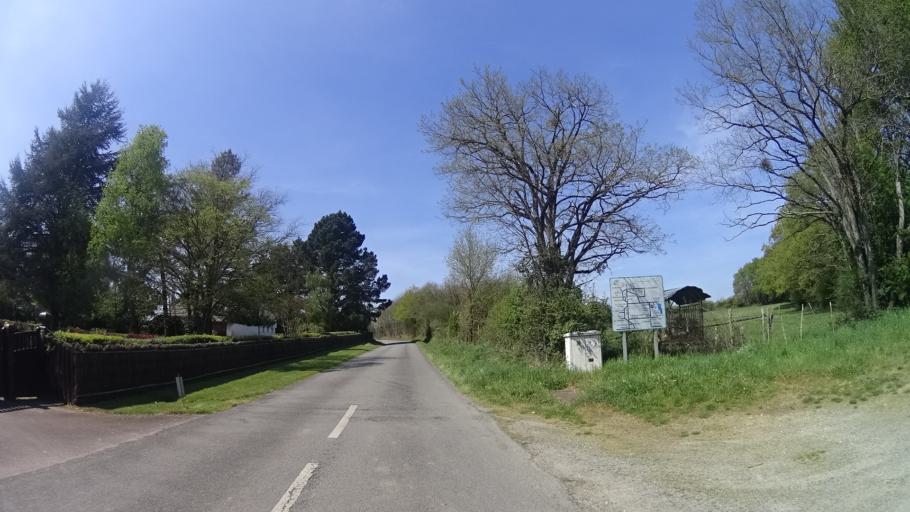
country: FR
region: Pays de la Loire
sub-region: Departement de la Loire-Atlantique
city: Fegreac
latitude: 47.5917
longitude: -2.0430
